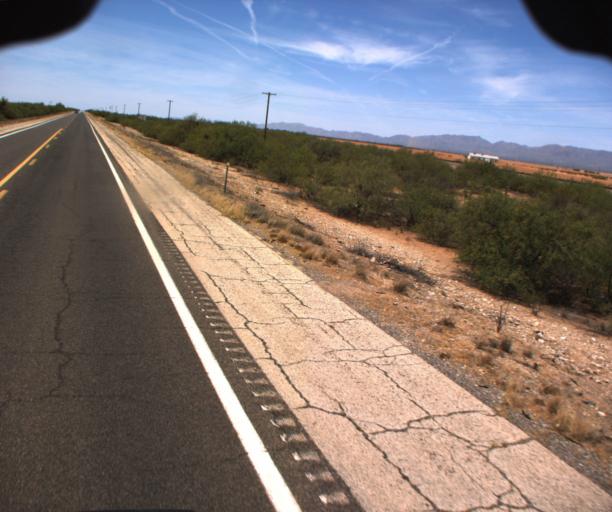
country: US
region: Arizona
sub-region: Yavapai County
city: Congress
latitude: 33.9380
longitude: -113.1968
